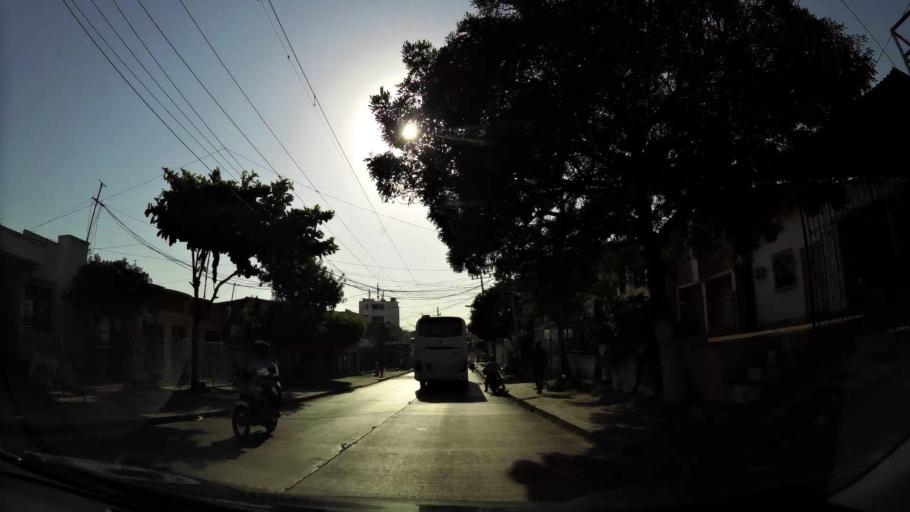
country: CO
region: Bolivar
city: Cartagena
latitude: 10.4007
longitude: -75.5019
